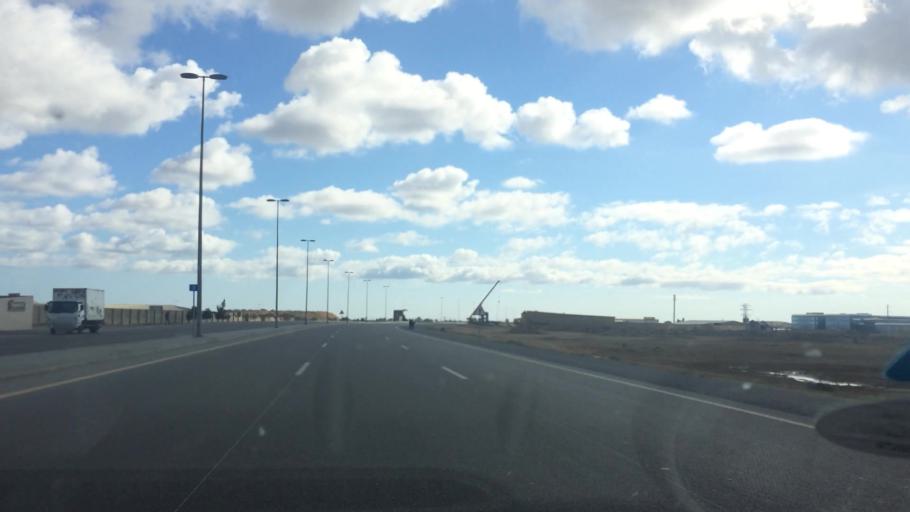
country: AZ
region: Baki
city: Qala
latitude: 40.4576
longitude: 50.1373
